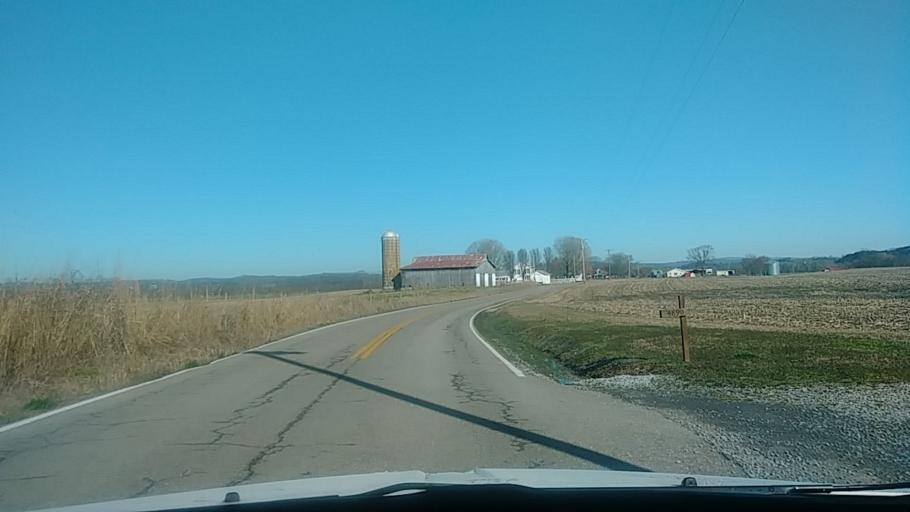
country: US
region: Tennessee
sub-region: Jefferson County
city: White Pine
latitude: 36.1574
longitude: -83.1617
